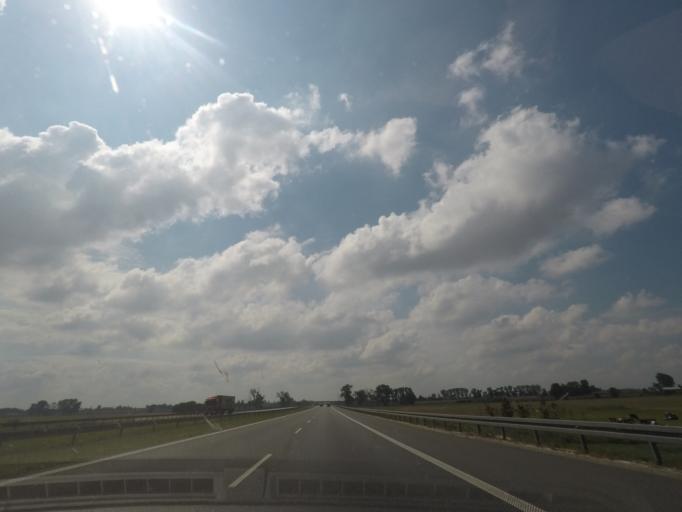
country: PL
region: Lodz Voivodeship
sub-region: Powiat kutnowski
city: Krzyzanow
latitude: 52.1784
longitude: 19.4862
